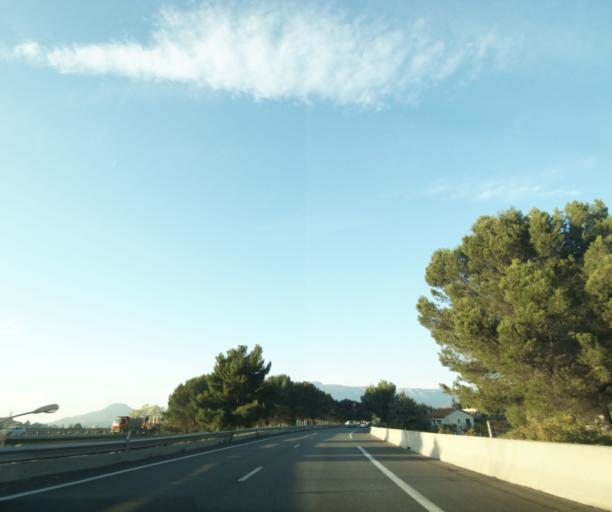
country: FR
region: Provence-Alpes-Cote d'Azur
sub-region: Departement des Bouches-du-Rhone
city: Aubagne
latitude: 43.2799
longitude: 5.5850
